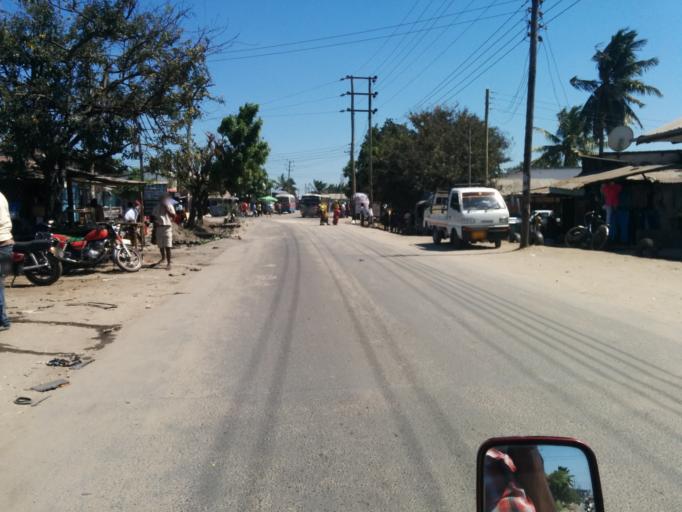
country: TZ
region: Dar es Salaam
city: Magomeni
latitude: -6.7907
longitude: 39.2340
